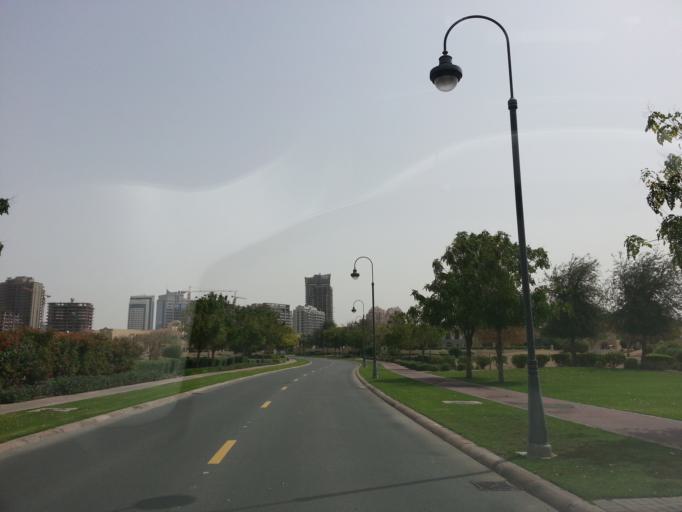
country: AE
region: Dubai
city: Dubai
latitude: 25.0366
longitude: 55.2119
